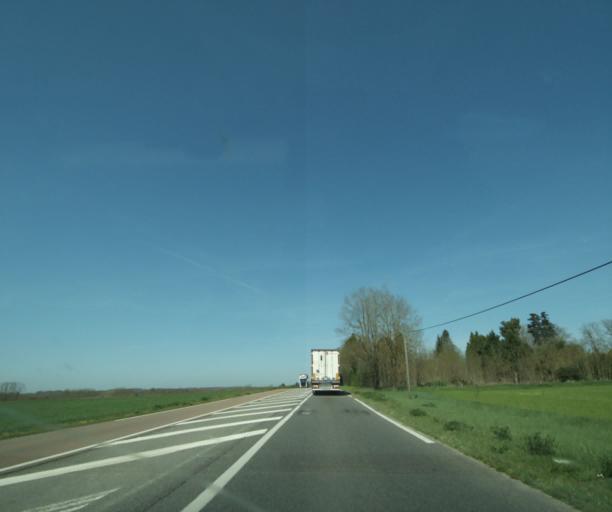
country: FR
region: Bourgogne
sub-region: Departement de la Nievre
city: Chantenay-Saint-Imbert
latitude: 46.7388
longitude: 3.1618
